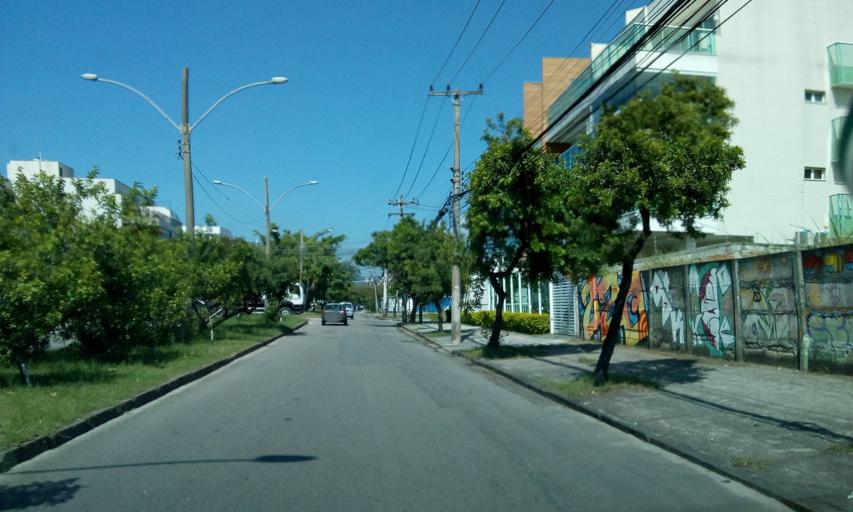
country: BR
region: Rio de Janeiro
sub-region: Nilopolis
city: Nilopolis
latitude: -23.0175
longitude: -43.4628
